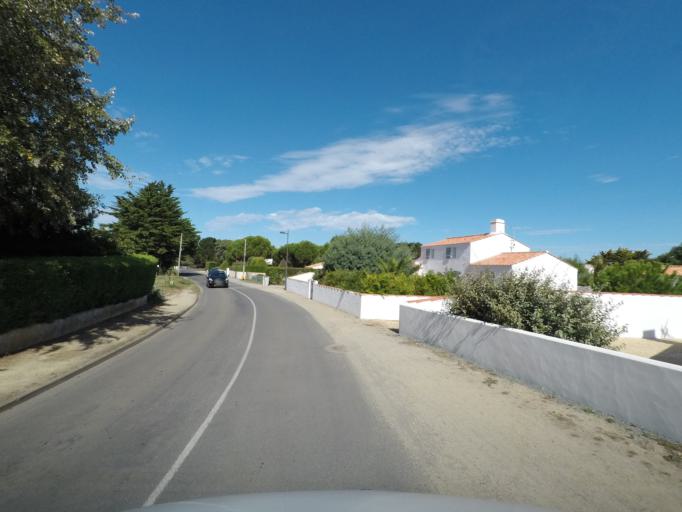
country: FR
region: Pays de la Loire
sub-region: Departement de la Vendee
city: La Gueriniere
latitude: 46.9991
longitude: -2.2252
